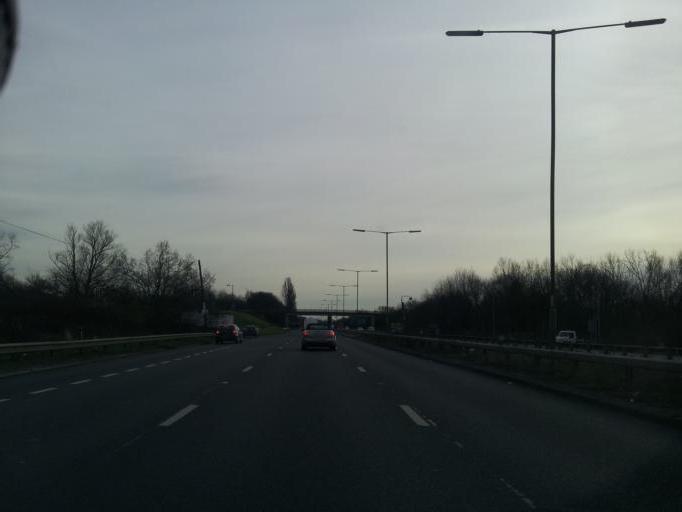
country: GB
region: England
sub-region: Hertfordshire
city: Borehamwood
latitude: 51.6568
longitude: -0.2491
